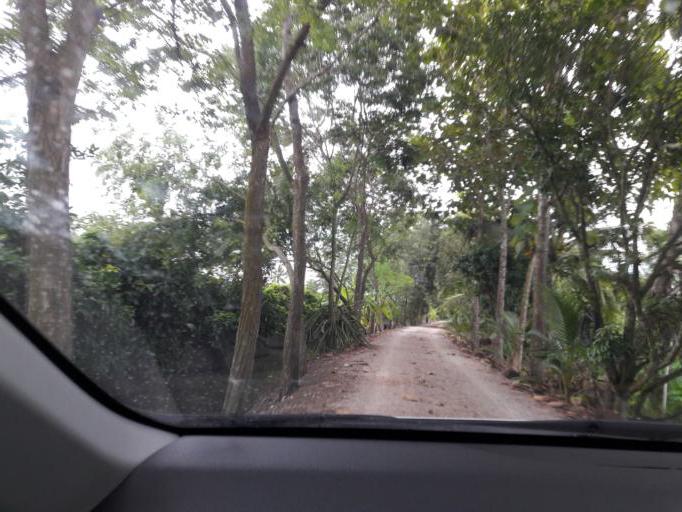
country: TH
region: Ratchaburi
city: Damnoen Saduak
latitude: 13.5452
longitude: 99.9992
